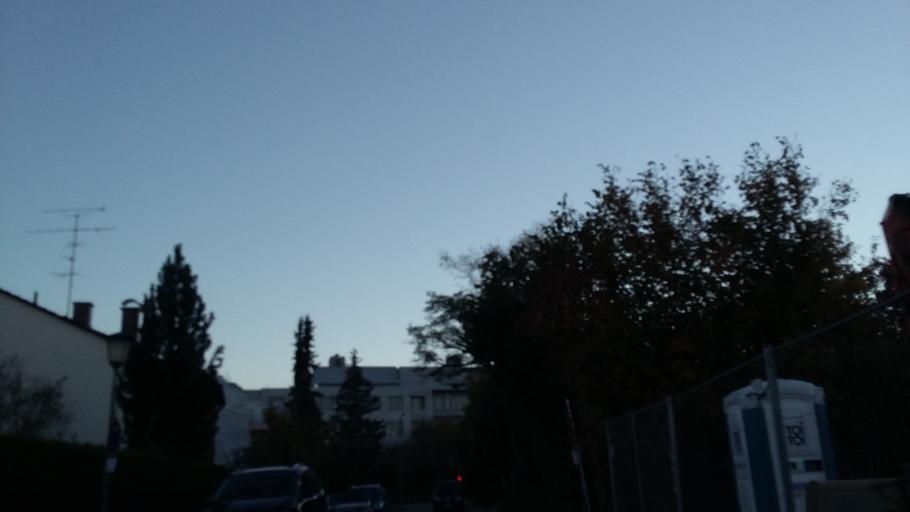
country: DE
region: Bavaria
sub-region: Upper Bavaria
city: Neuried
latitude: 48.1157
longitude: 11.4673
